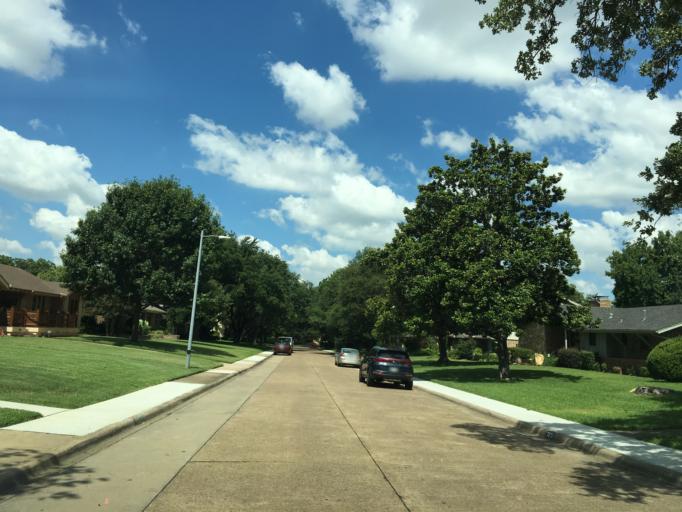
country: US
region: Texas
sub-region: Dallas County
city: Farmers Branch
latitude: 32.9218
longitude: -96.8579
